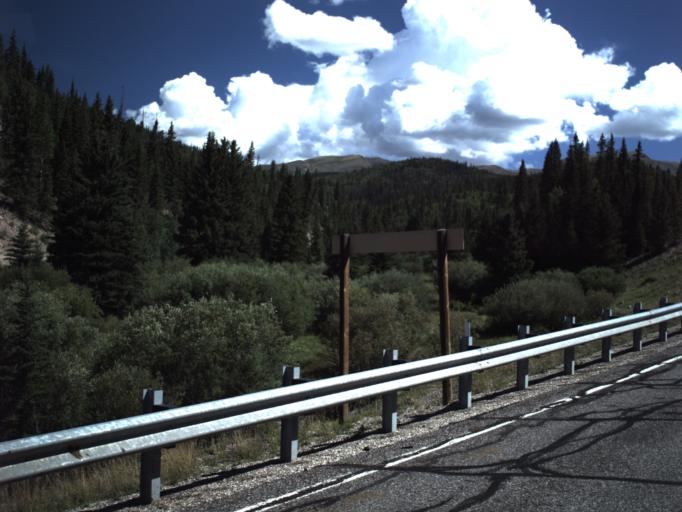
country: US
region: Utah
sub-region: Piute County
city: Junction
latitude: 38.3057
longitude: -112.4181
